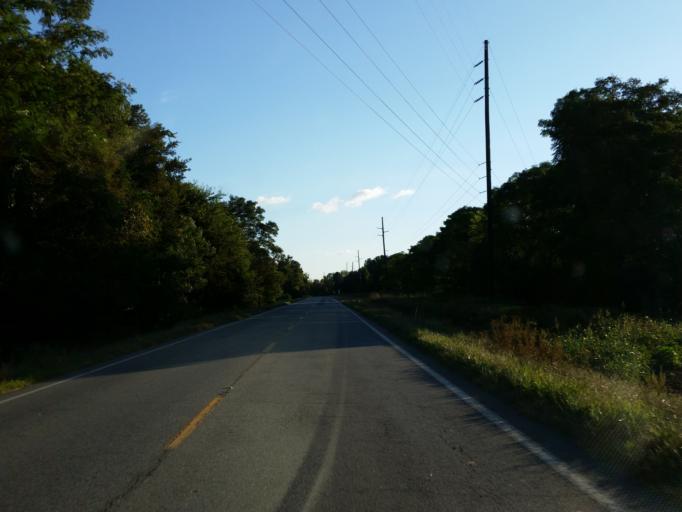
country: US
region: Georgia
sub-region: Dooly County
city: Vienna
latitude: 32.1141
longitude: -83.7719
